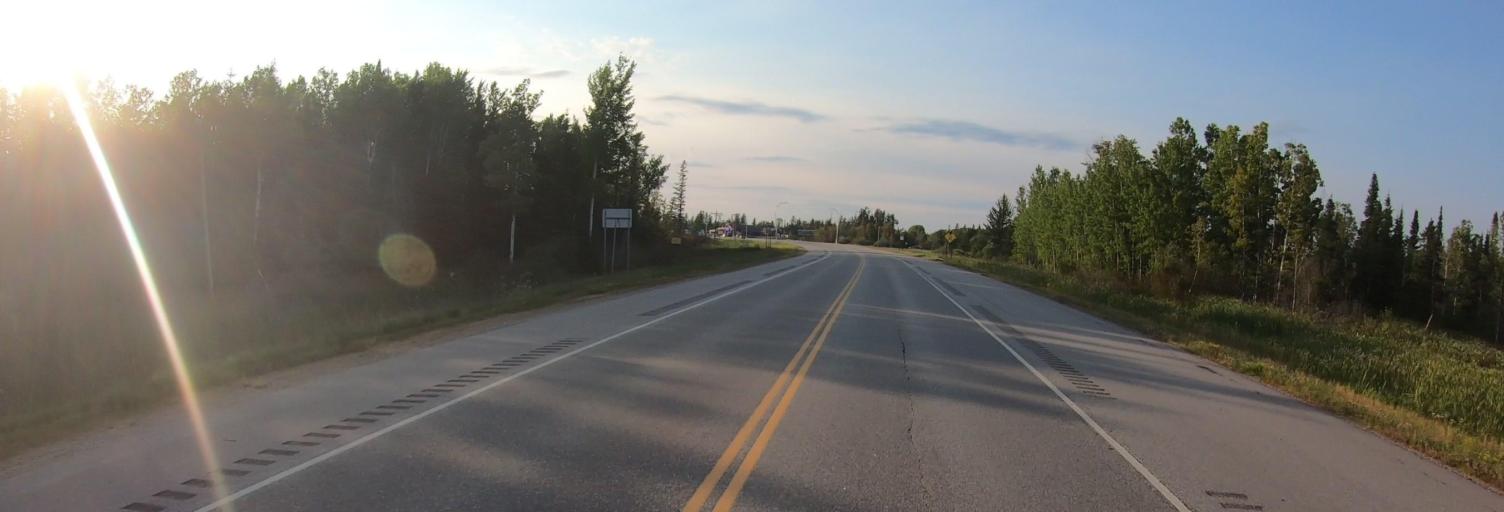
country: US
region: Minnesota
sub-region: Saint Louis County
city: Mountain Iron
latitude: 47.8403
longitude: -92.6777
